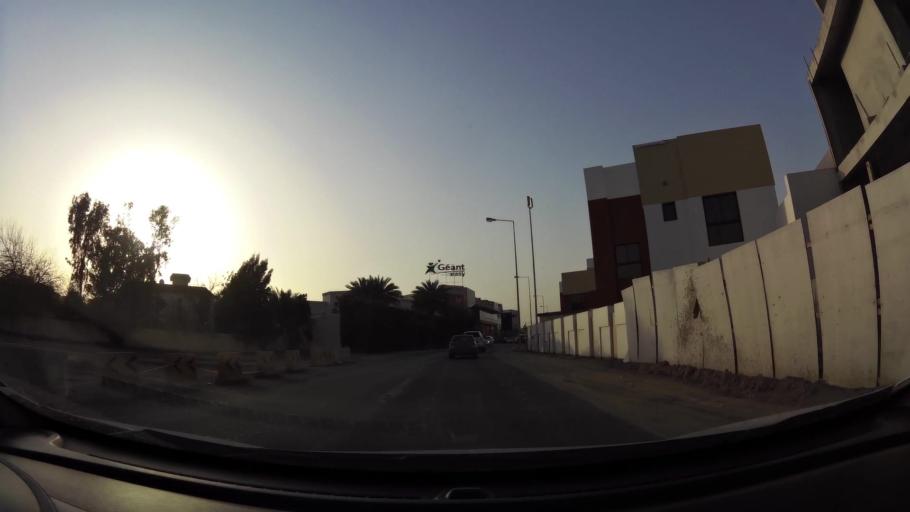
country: BH
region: Manama
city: Jidd Hafs
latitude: 26.1996
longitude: 50.4997
